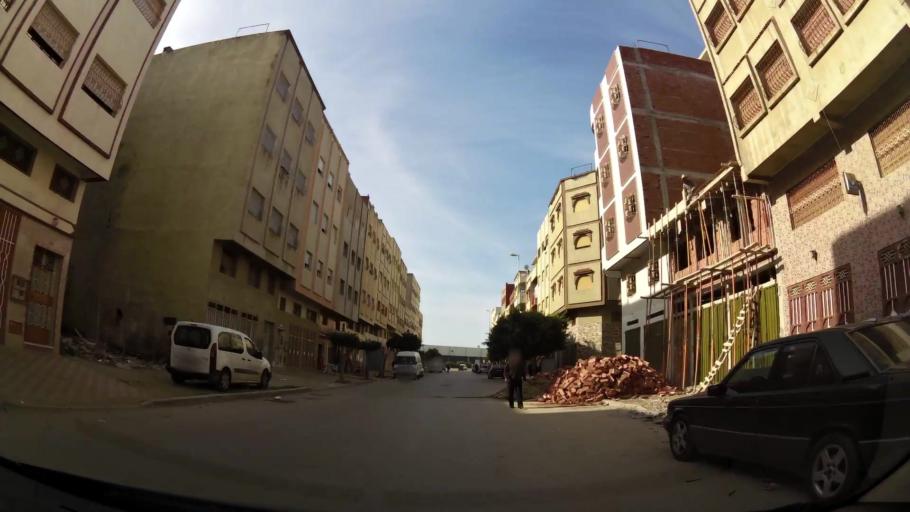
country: MA
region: Tanger-Tetouan
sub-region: Tanger-Assilah
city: Tangier
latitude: 35.7379
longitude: -5.7980
